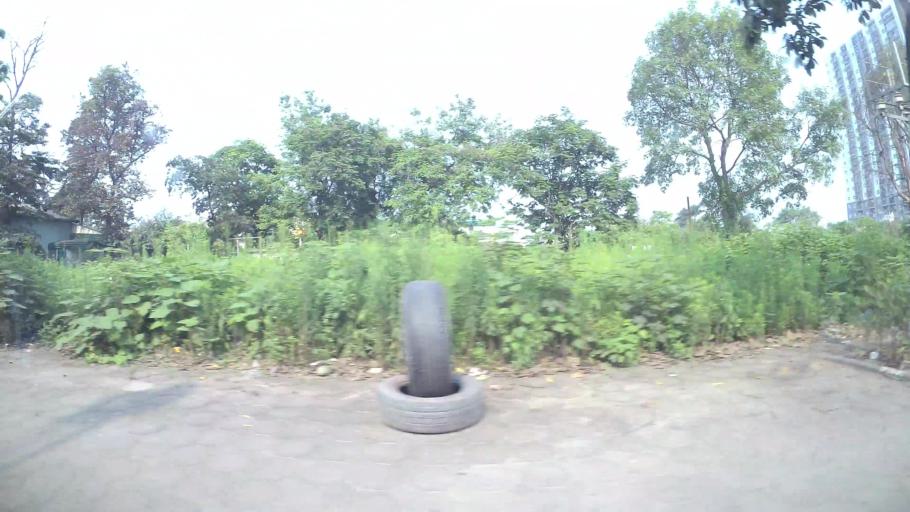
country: VN
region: Ha Noi
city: Thanh Xuan
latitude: 20.9761
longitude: 105.8248
